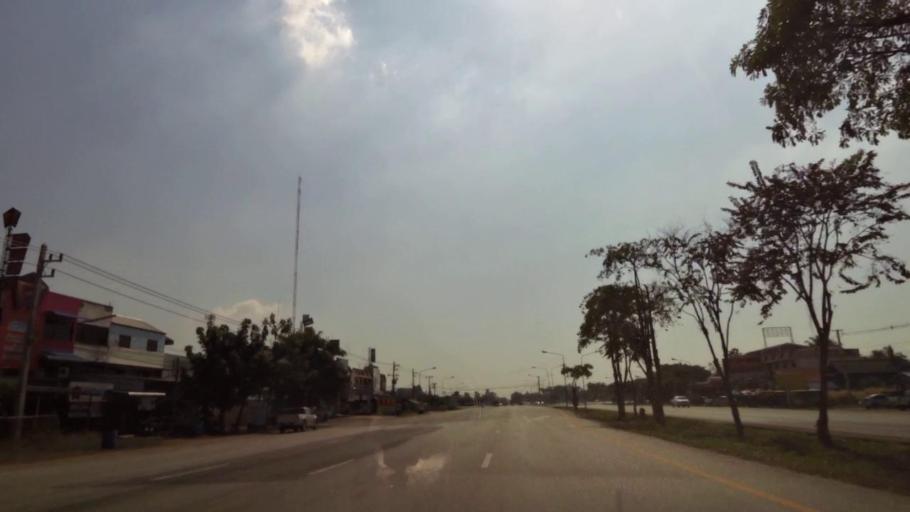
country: TH
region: Phichit
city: Bueng Na Rang
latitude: 16.1263
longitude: 100.1256
